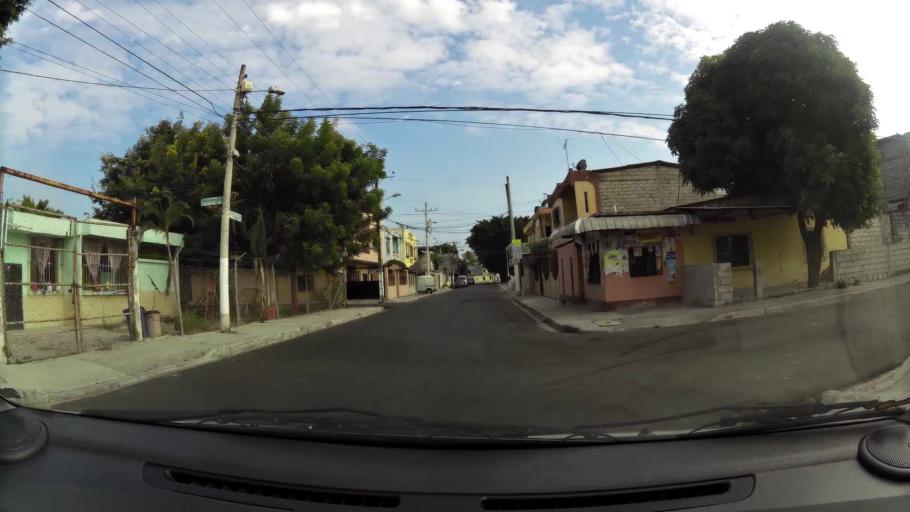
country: EC
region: Guayas
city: Guayaquil
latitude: -2.2453
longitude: -79.8839
